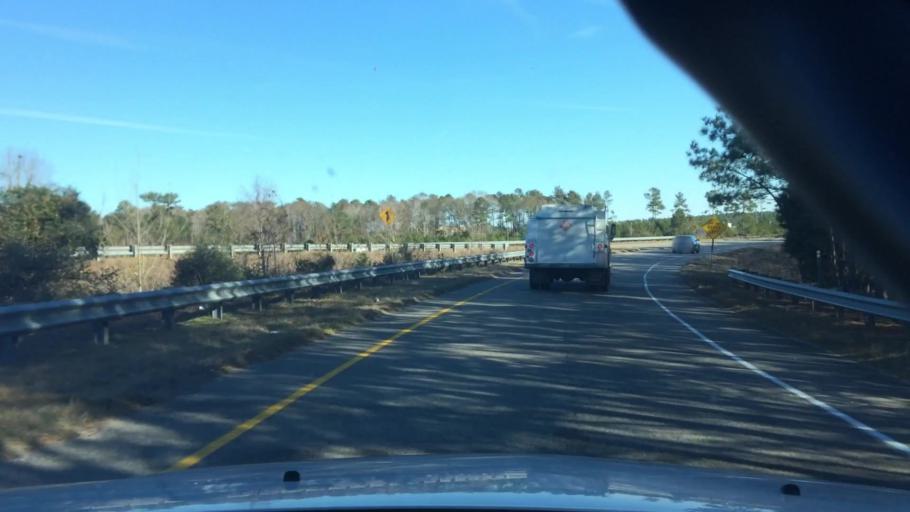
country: US
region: South Carolina
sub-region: Horry County
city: Myrtle Beach
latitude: 33.7536
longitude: -78.8508
